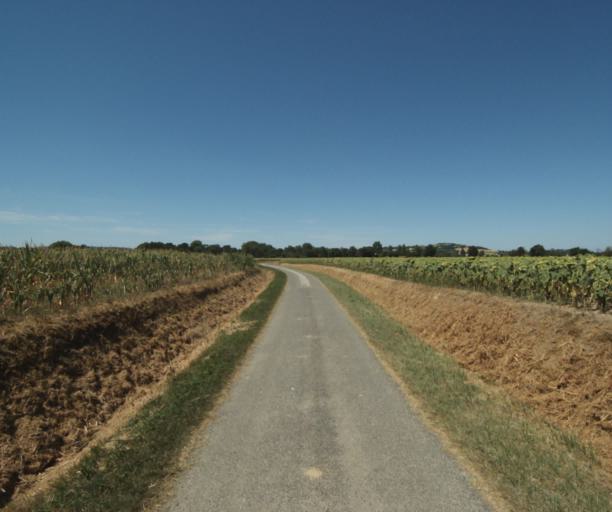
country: FR
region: Midi-Pyrenees
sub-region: Departement de la Haute-Garonne
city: Revel
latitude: 43.4762
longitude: 1.9486
